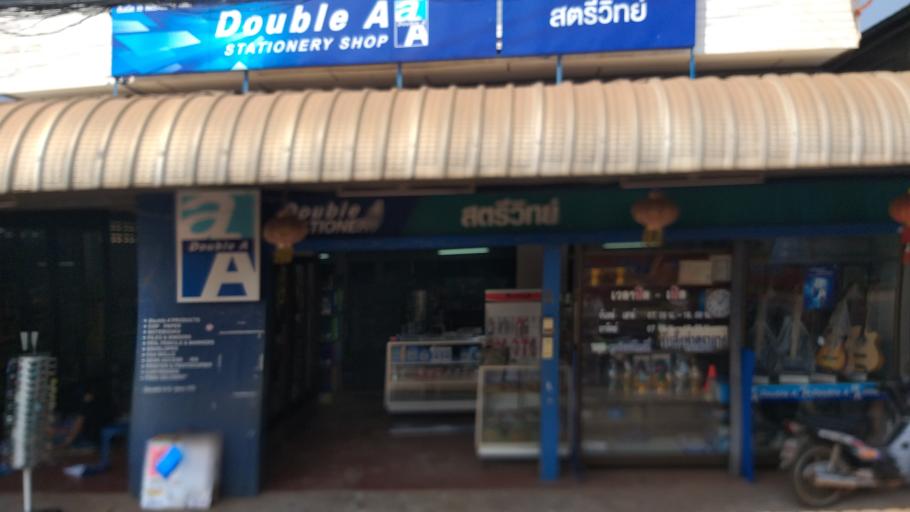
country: TH
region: Changwat Udon Thani
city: Nong Han
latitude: 17.3632
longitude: 103.1093
